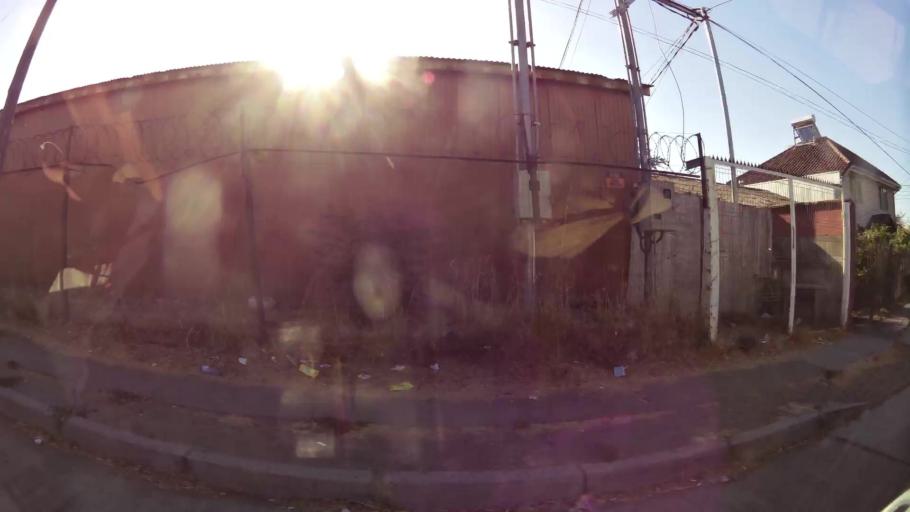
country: CL
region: Maule
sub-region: Provincia de Talca
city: Talca
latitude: -35.4343
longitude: -71.6711
